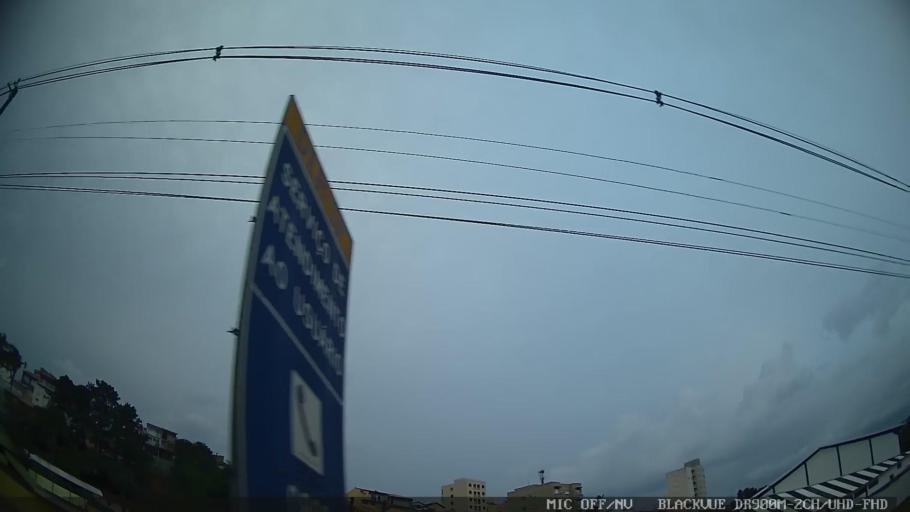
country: BR
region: Sao Paulo
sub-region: Braganca Paulista
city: Braganca Paulista
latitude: -22.9519
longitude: -46.5502
